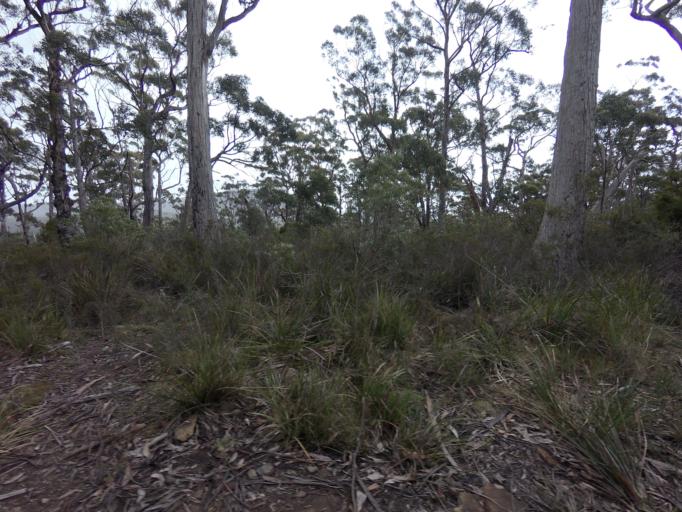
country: AU
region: Tasmania
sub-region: Huon Valley
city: Geeveston
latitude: -43.4644
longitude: 146.9184
